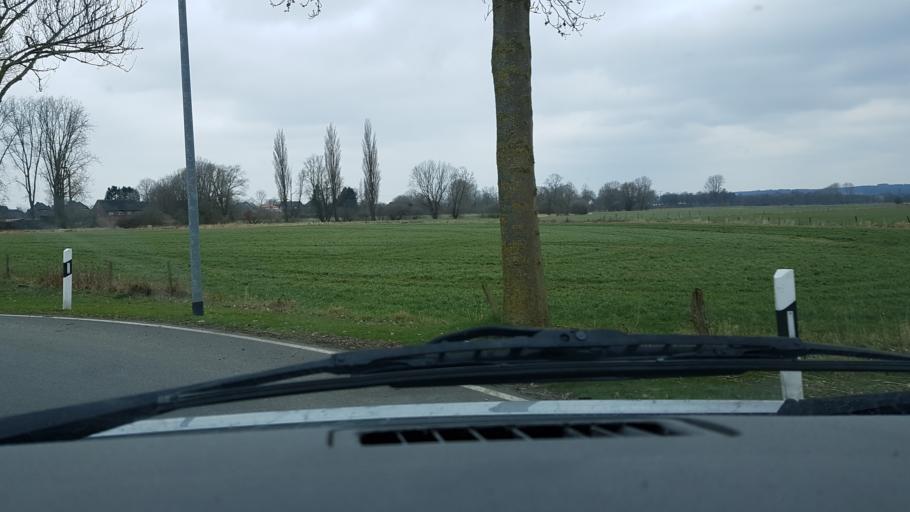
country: DE
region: North Rhine-Westphalia
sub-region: Regierungsbezirk Dusseldorf
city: Kranenburg
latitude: 51.7943
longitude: 6.0057
